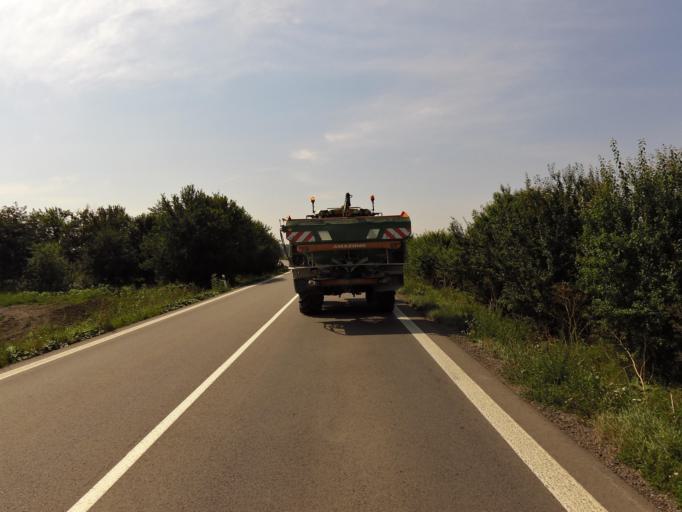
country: CZ
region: Central Bohemia
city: Prerov nad Labem
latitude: 50.1568
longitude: 14.8503
